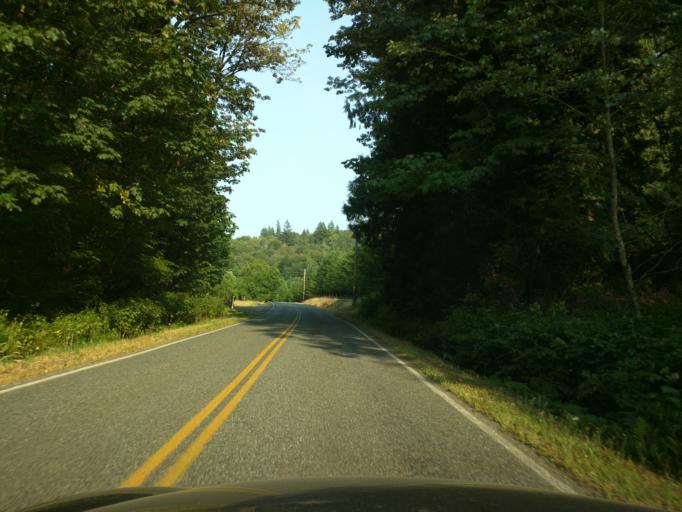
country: US
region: Washington
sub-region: Whatcom County
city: Peaceful Valley
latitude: 48.9629
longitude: -122.1774
